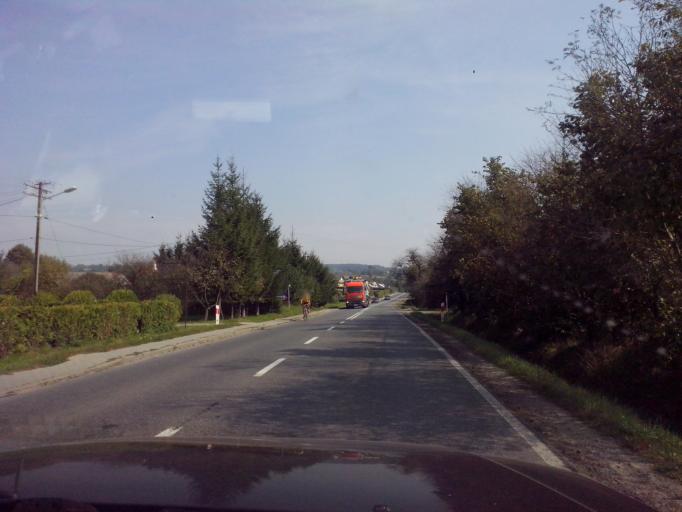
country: PL
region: Subcarpathian Voivodeship
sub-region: Powiat strzyzowski
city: Czudec
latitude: 49.9425
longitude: 21.8192
